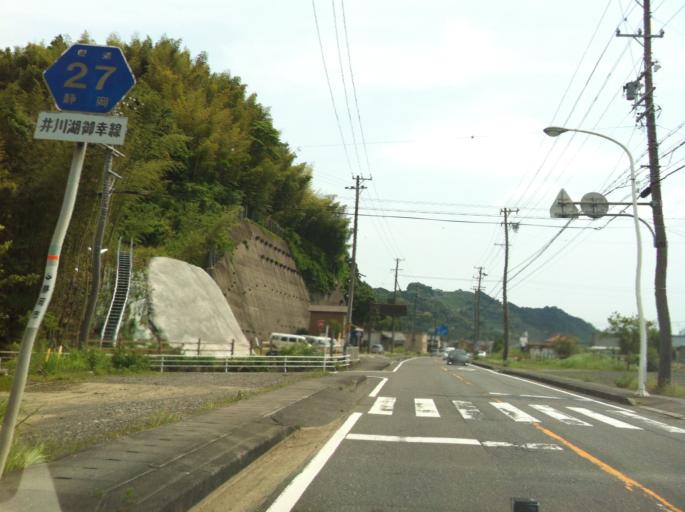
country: JP
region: Shizuoka
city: Shizuoka-shi
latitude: 35.0380
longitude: 138.3799
